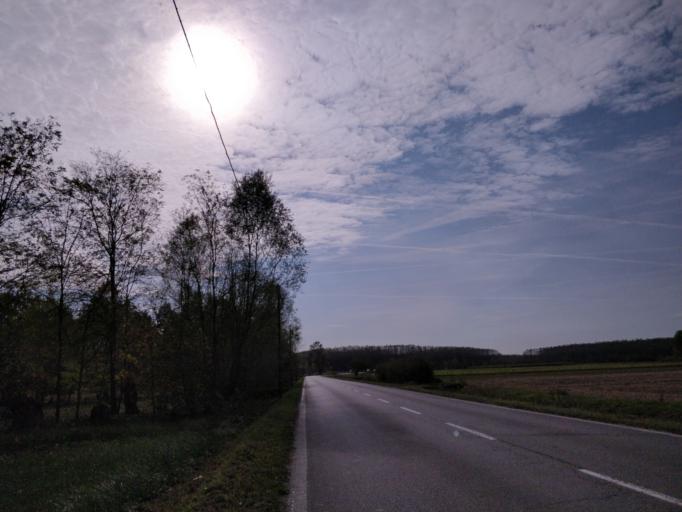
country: IT
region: Friuli Venezia Giulia
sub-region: Provincia di Udine
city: Bertiolo
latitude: 45.9169
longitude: 13.0478
